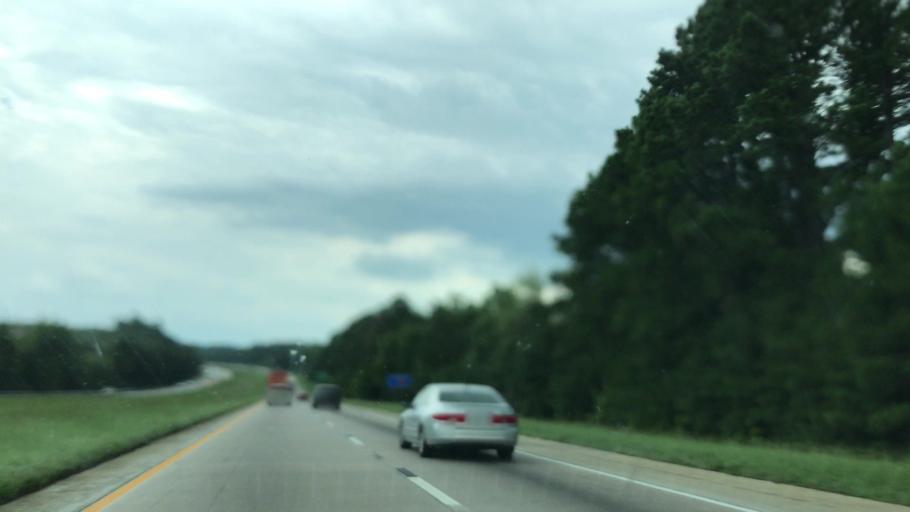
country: US
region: South Carolina
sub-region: Fairfield County
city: Winnsboro Mills
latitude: 34.3302
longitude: -81.0051
